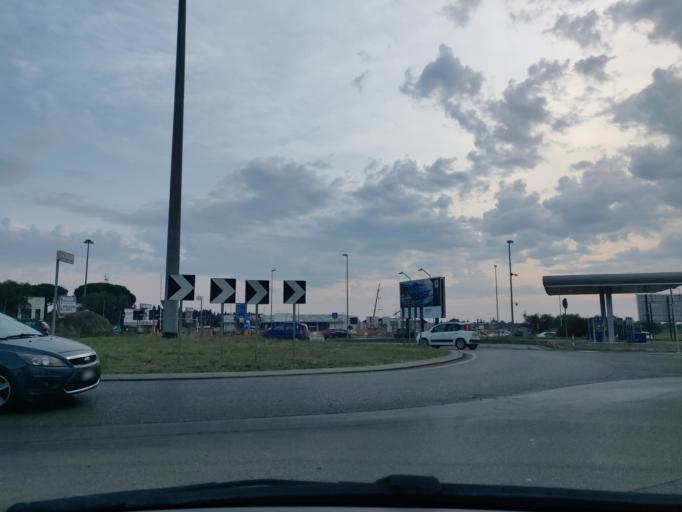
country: IT
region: Latium
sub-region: Provincia di Viterbo
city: Viterbo
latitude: 42.4375
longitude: 12.0951
